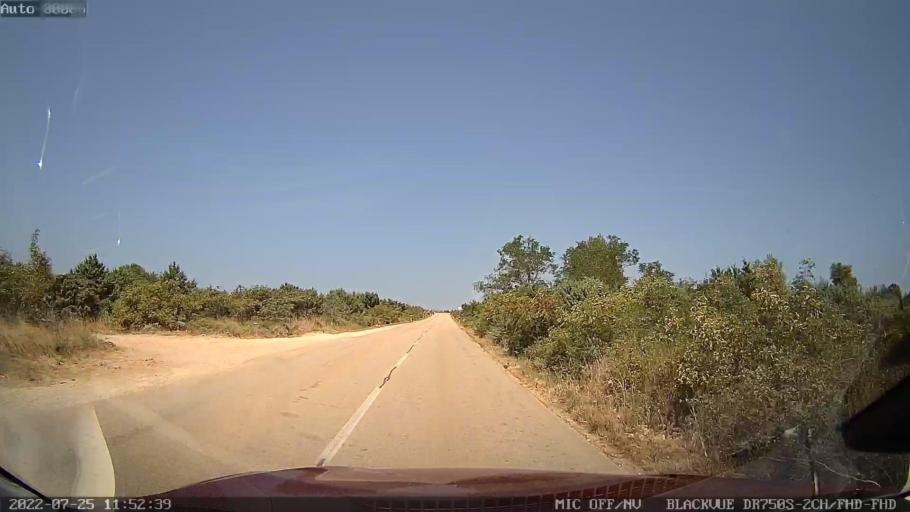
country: HR
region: Zadarska
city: Vrsi
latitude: 44.2494
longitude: 15.2415
